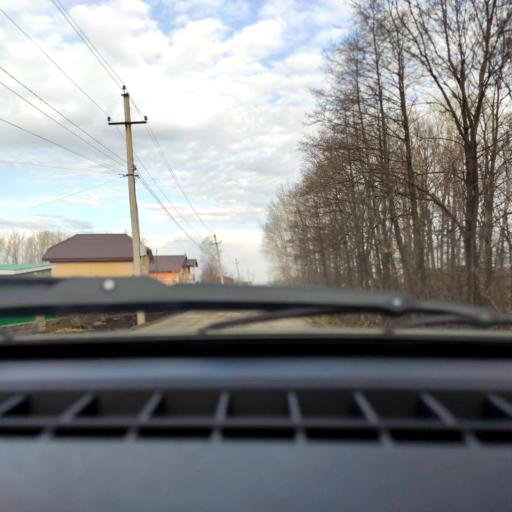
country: RU
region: Bashkortostan
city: Ufa
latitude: 54.6291
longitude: 55.8901
